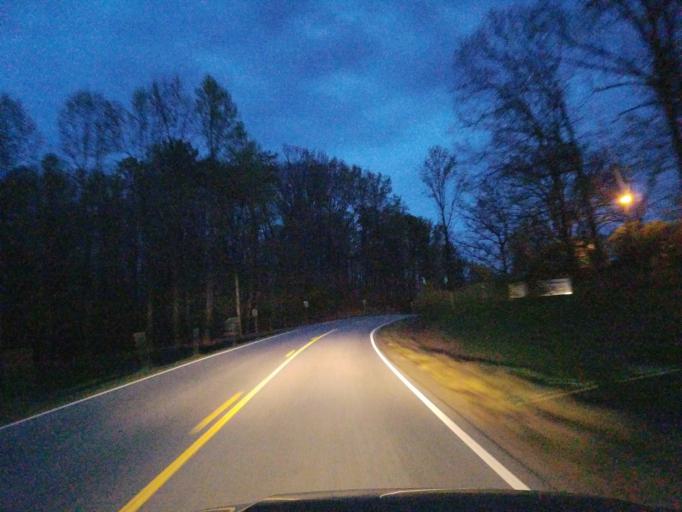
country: US
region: Georgia
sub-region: Lumpkin County
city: Dahlonega
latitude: 34.5744
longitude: -83.9674
